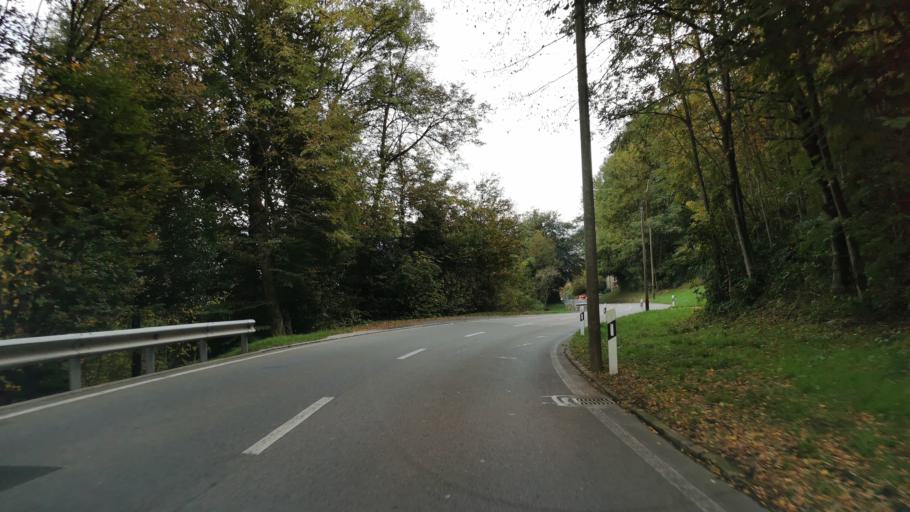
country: CH
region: Ticino
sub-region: Lugano District
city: Pura
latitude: 45.9946
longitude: 8.8650
